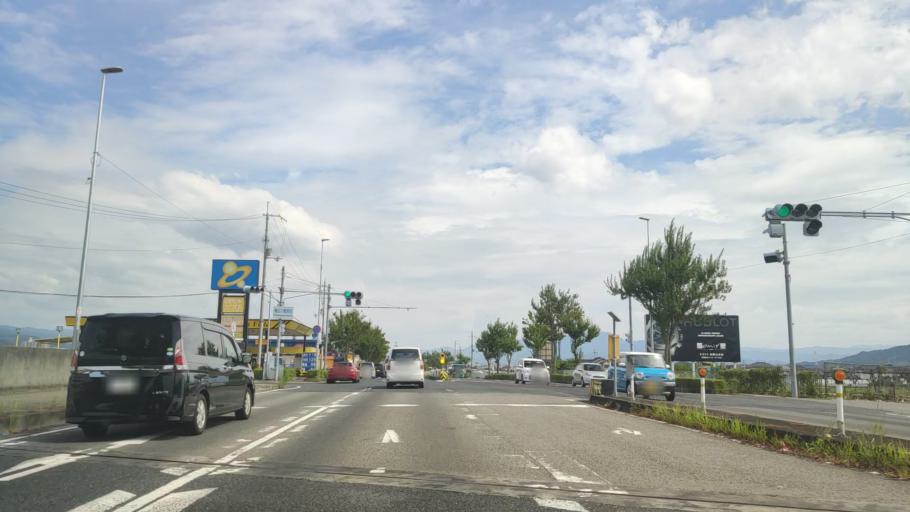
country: JP
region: Wakayama
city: Iwade
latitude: 34.2639
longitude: 135.2762
